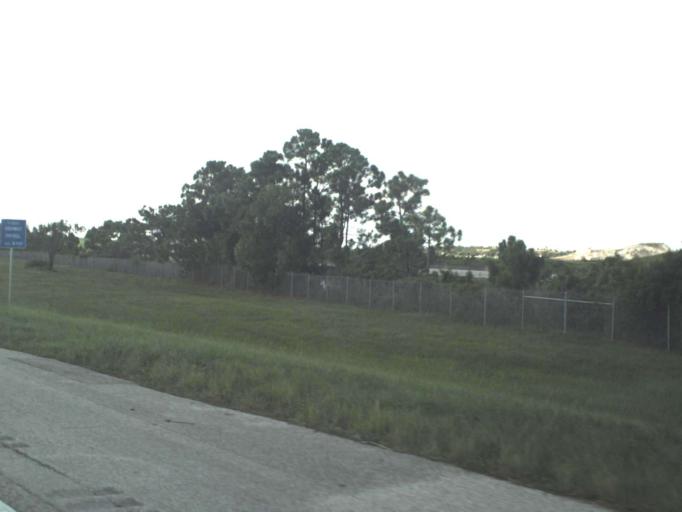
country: US
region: Florida
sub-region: Palm Beach County
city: Limestone Creek
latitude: 26.9497
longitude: -80.1613
